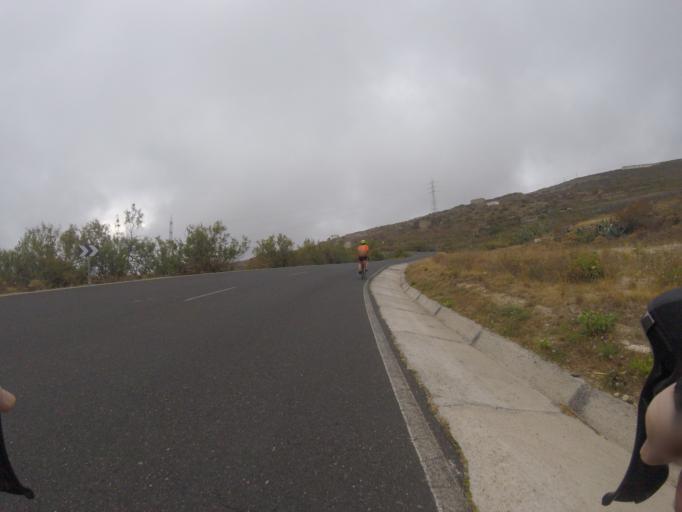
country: ES
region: Canary Islands
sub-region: Provincia de Santa Cruz de Tenerife
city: Guimar
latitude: 28.2933
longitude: -16.4027
